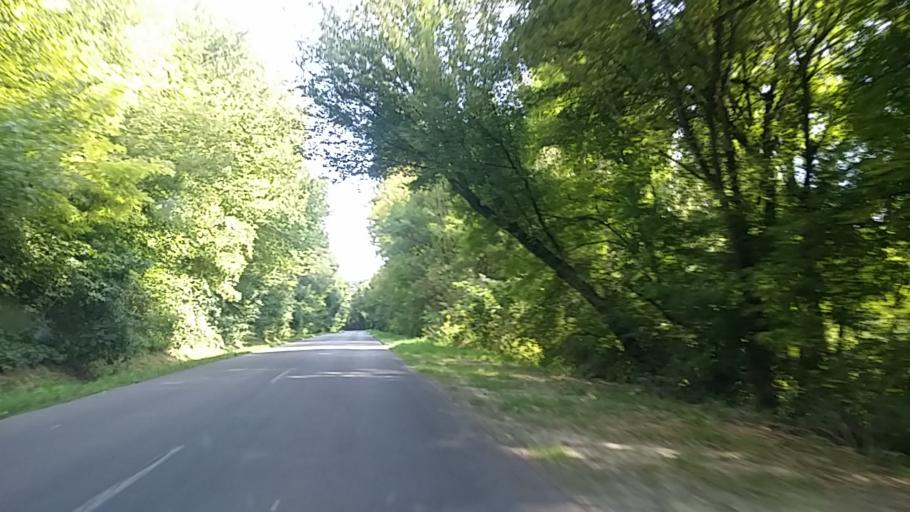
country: HU
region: Tolna
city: Gyonk
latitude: 46.5409
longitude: 18.4949
